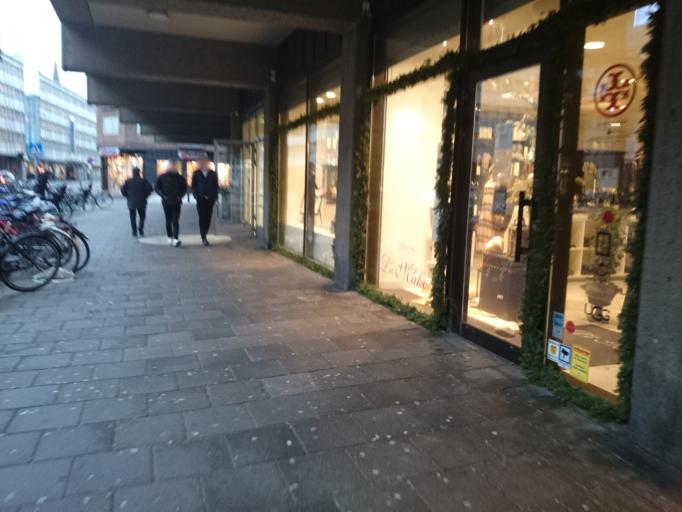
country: SE
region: Skane
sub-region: Malmo
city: Malmoe
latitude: 55.6033
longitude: 13.0050
